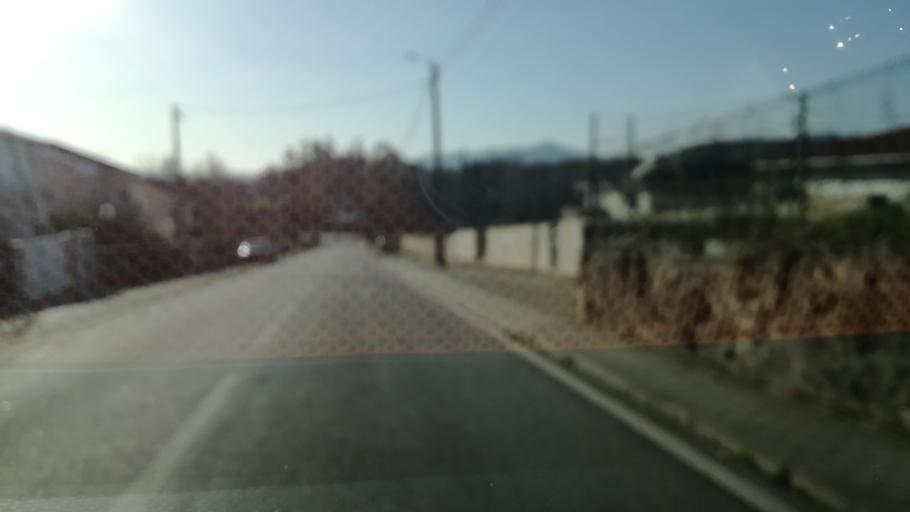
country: PT
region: Braga
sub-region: Guimaraes
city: Ponte
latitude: 41.5140
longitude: -8.3138
